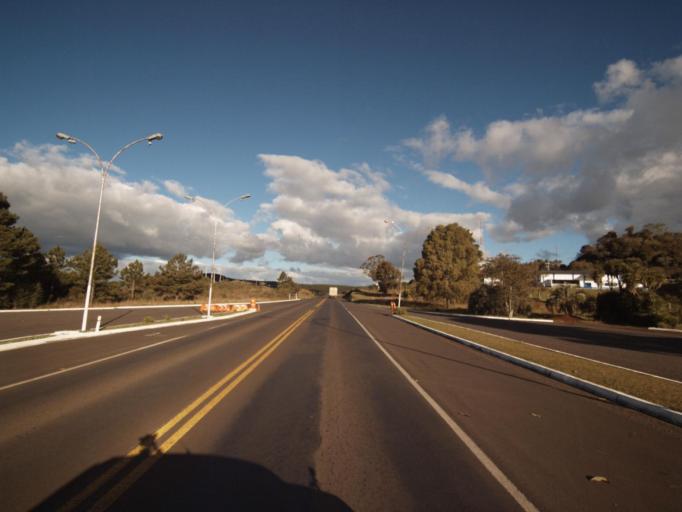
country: BR
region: Santa Catarina
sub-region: Campos Novos
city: Campos Novos
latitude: -27.3519
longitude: -51.3348
